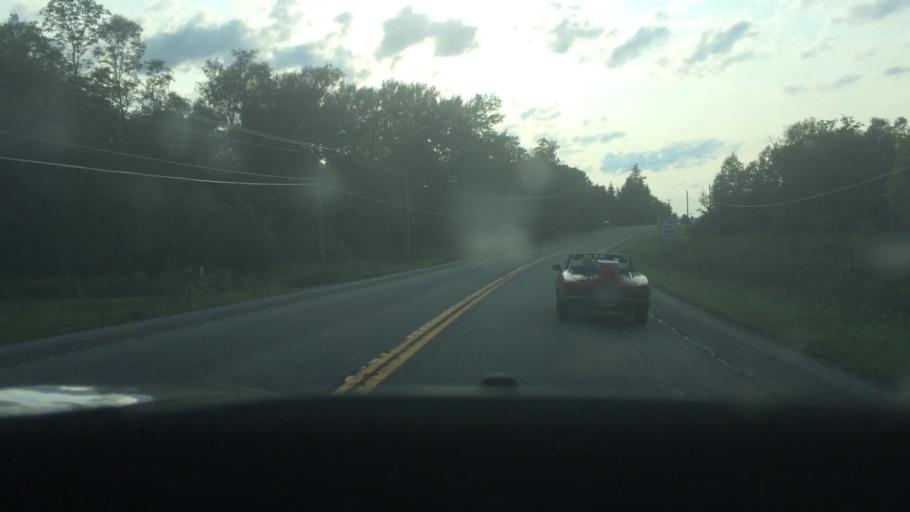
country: US
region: New York
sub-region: St. Lawrence County
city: Ogdensburg
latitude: 44.6659
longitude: -75.3645
